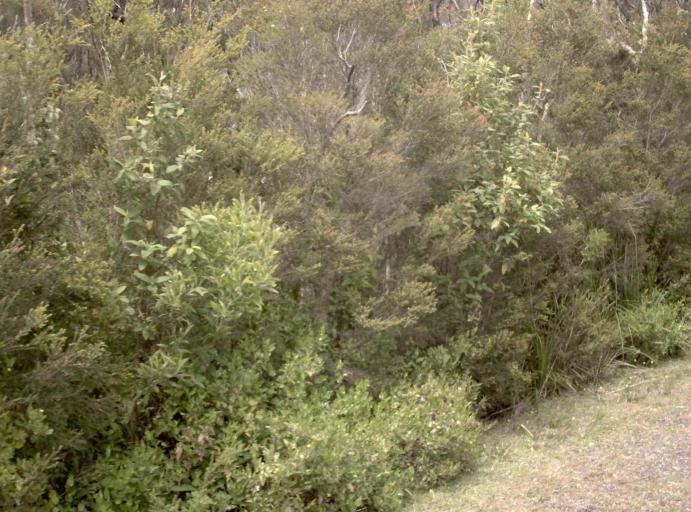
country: AU
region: Victoria
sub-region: Latrobe
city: Morwell
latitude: -39.0171
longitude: 146.3118
